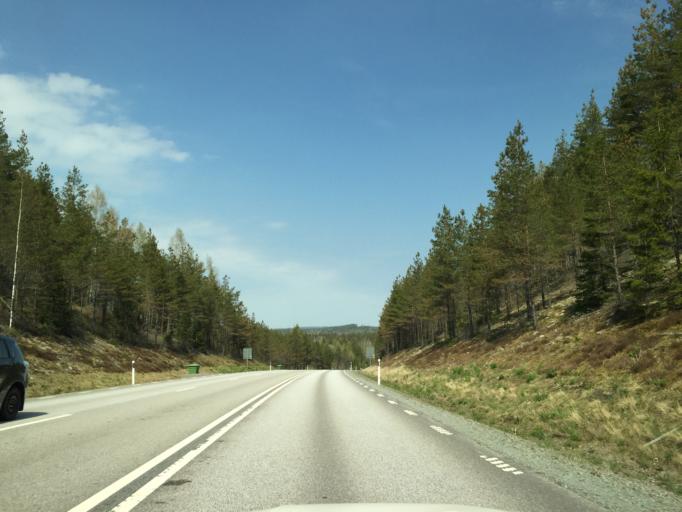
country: SE
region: Vaestra Goetaland
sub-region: Bengtsfors Kommun
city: Dals Langed
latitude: 58.8499
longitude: 12.1676
